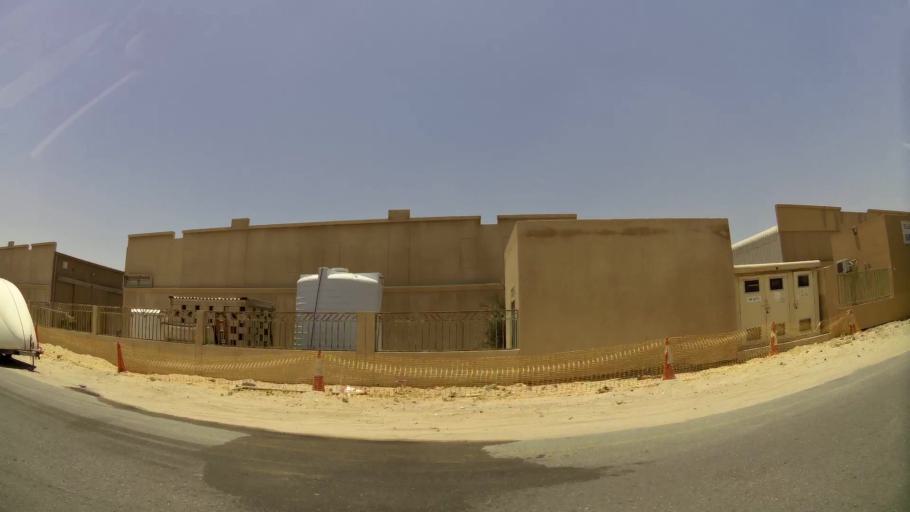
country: AE
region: Dubai
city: Dubai
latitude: 24.9855
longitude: 55.1680
